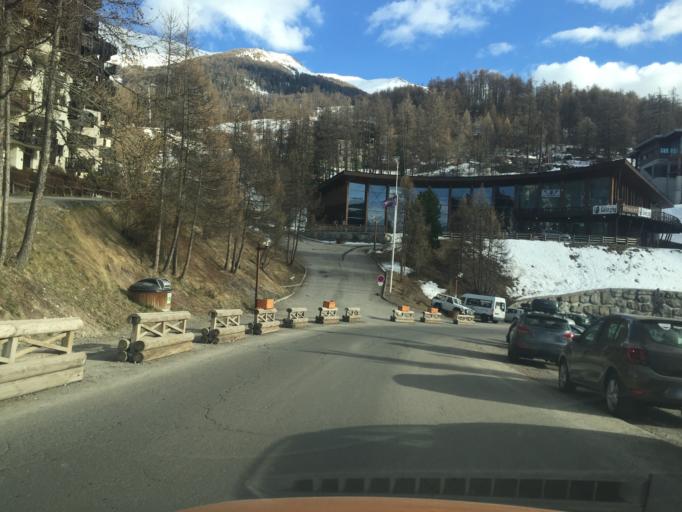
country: FR
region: Provence-Alpes-Cote d'Azur
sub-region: Departement des Hautes-Alpes
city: Embrun
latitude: 44.4926
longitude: 6.5559
